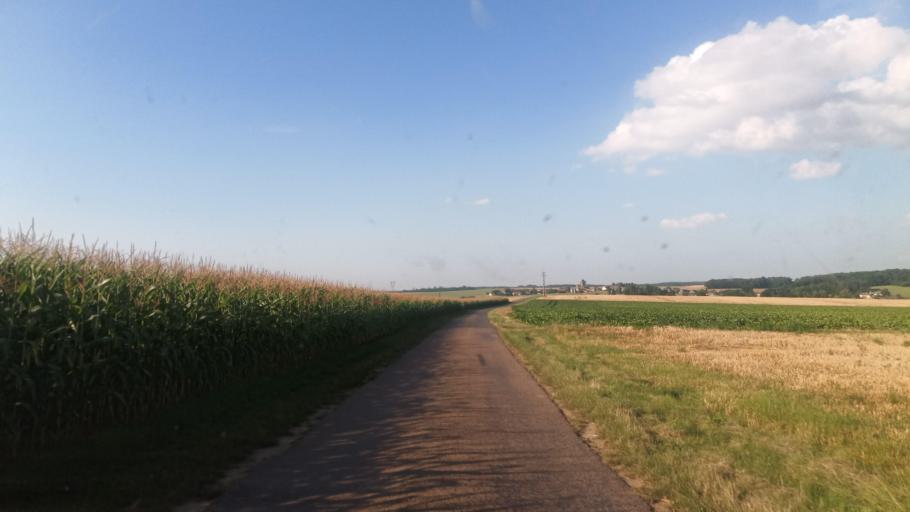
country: FR
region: Bourgogne
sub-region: Departement de l'Yonne
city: Saint-Valerien
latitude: 48.2259
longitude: 3.0880
